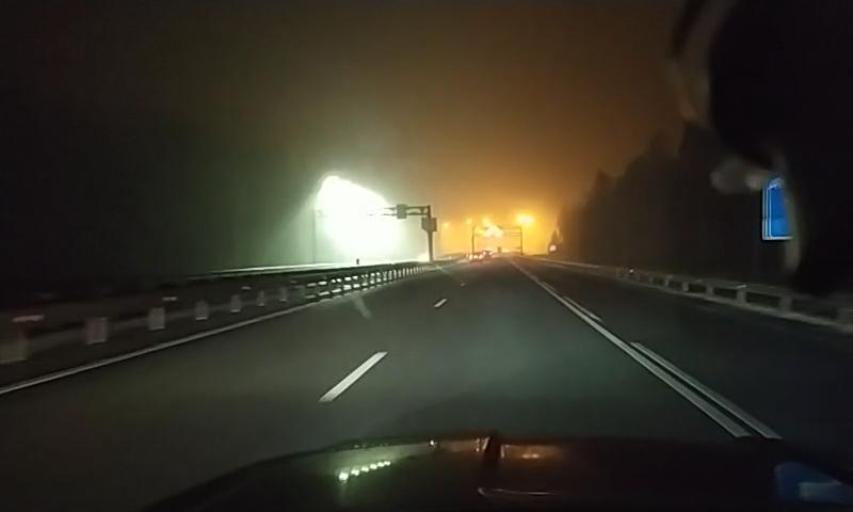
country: RU
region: Leningrad
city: Agalatovo
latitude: 60.2149
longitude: 30.3599
